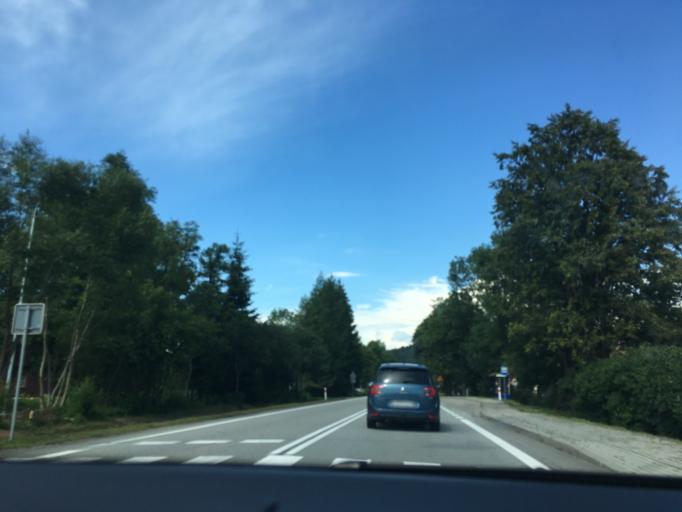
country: PL
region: Subcarpathian Voivodeship
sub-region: Powiat krosnienski
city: Jasliska
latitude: 49.4340
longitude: 21.6891
